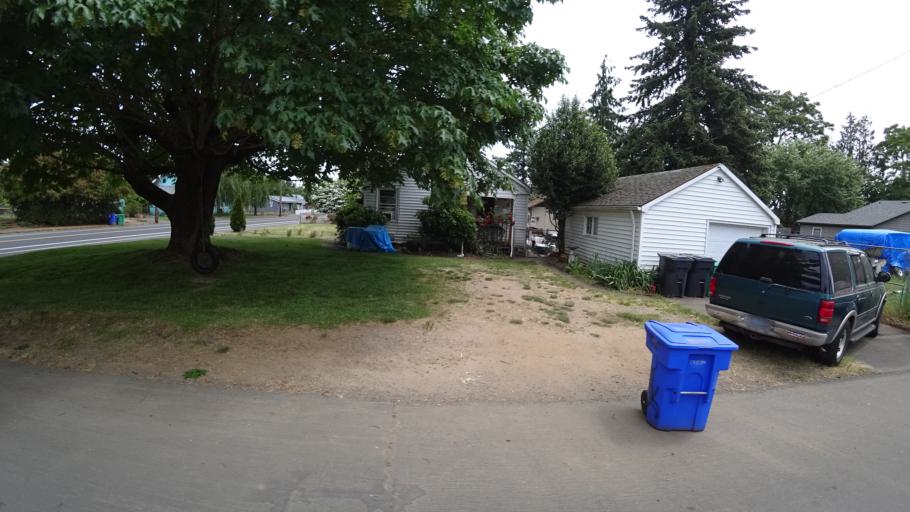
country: US
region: Oregon
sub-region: Multnomah County
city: Lents
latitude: 45.4757
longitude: -122.5913
